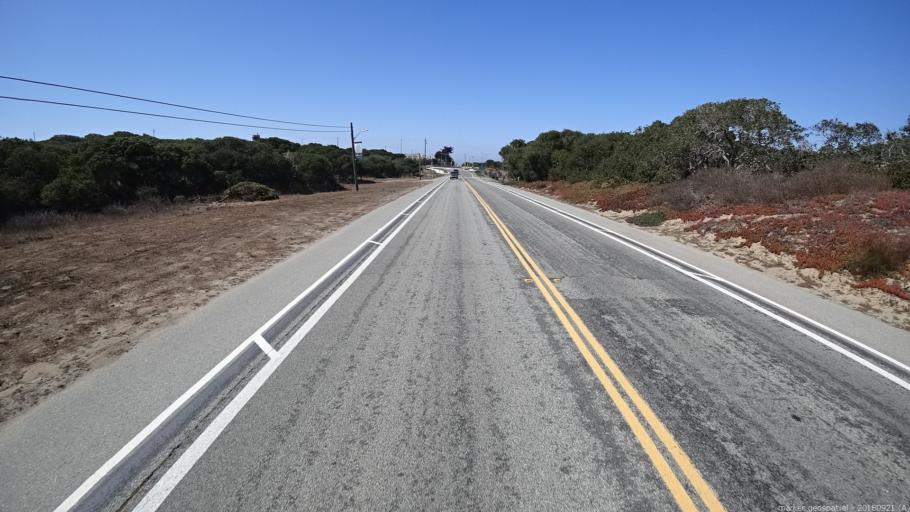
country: US
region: California
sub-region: Monterey County
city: Marina
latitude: 36.6547
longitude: -121.7836
